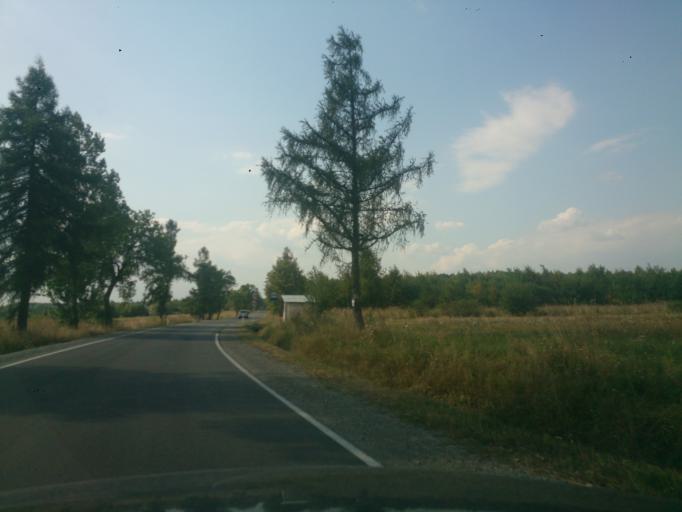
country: PL
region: Swietokrzyskie
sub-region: Powiat opatowski
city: Iwaniska
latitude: 50.6938
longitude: 21.3432
